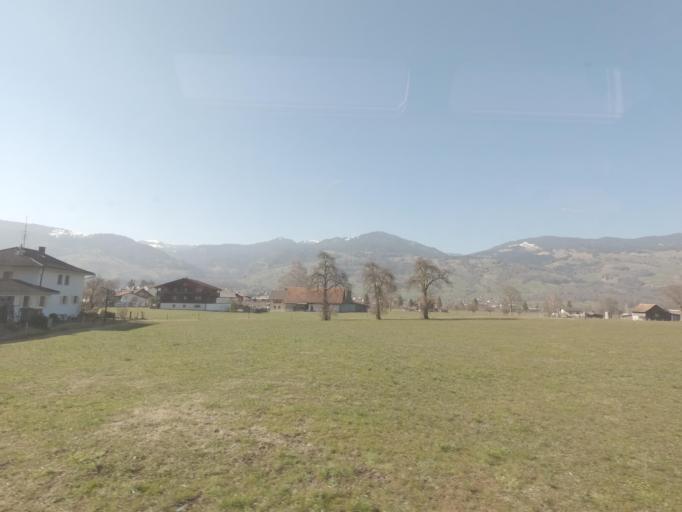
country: CH
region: Obwalden
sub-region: Obwalden
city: Giswil
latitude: 46.8403
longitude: 8.1891
